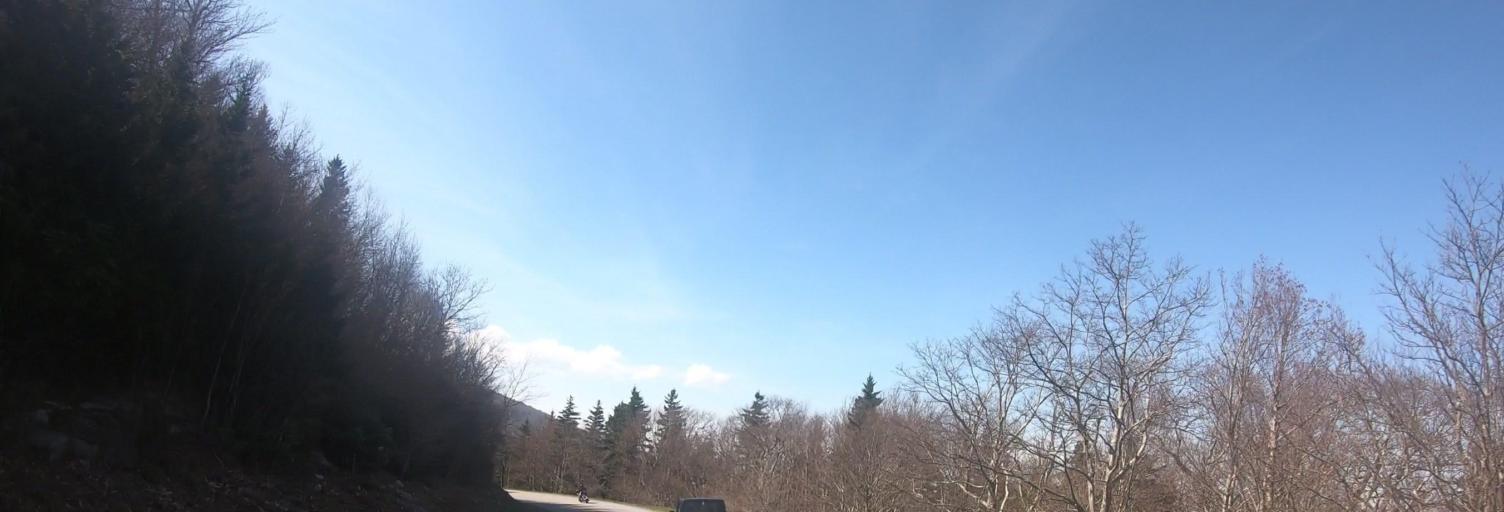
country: US
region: North Carolina
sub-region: Watauga County
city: Foscoe
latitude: 36.1015
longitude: -81.7786
